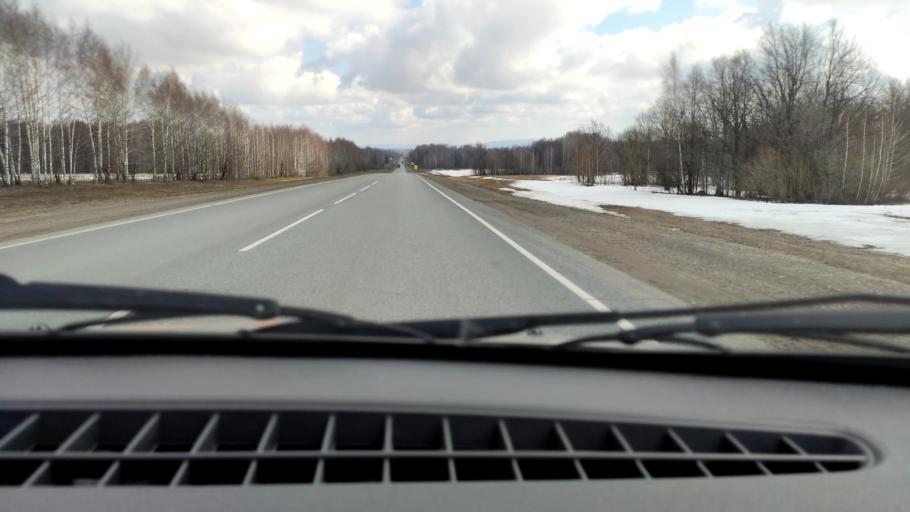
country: RU
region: Bashkortostan
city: Kudeyevskiy
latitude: 54.8109
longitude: 56.6585
